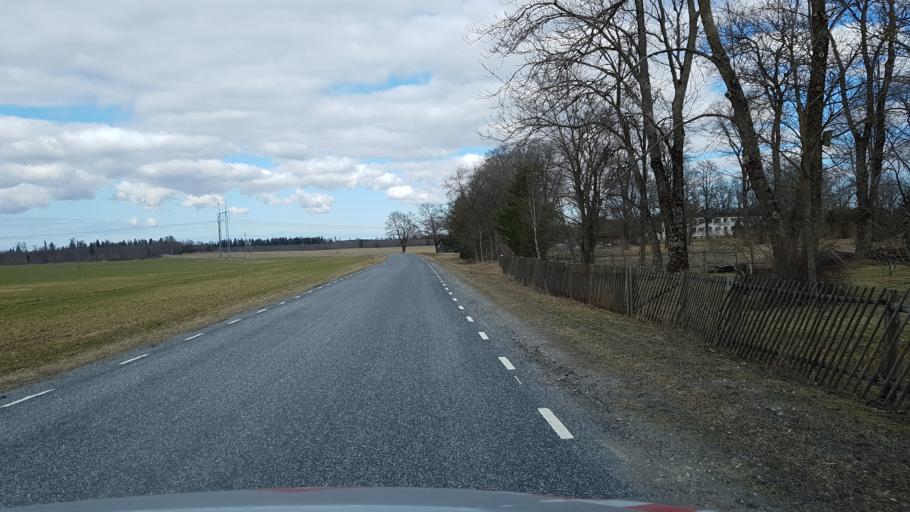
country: EE
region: Laeaene-Virumaa
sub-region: Tamsalu vald
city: Tamsalu
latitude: 59.1764
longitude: 26.1255
